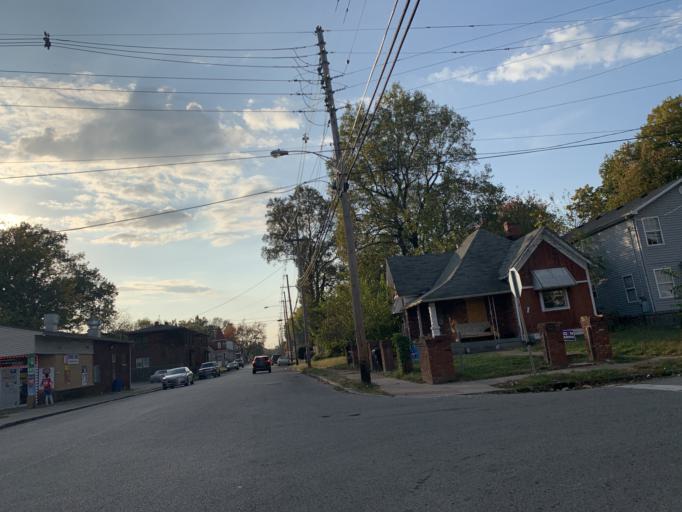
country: US
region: Kentucky
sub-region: Jefferson County
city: Shively
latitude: 38.2320
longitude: -85.8036
